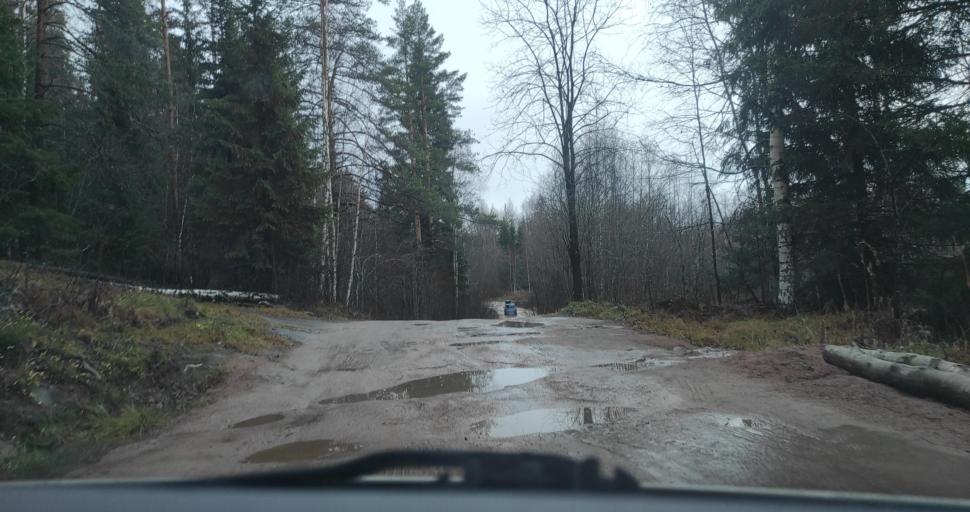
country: RU
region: Republic of Karelia
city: Pitkyaranta
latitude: 61.7462
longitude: 31.3957
